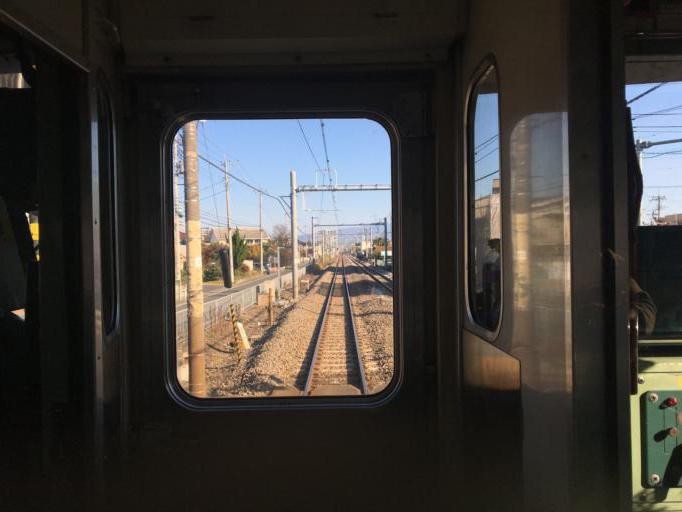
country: JP
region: Gunma
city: Takasaki
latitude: 36.3380
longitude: 139.0128
